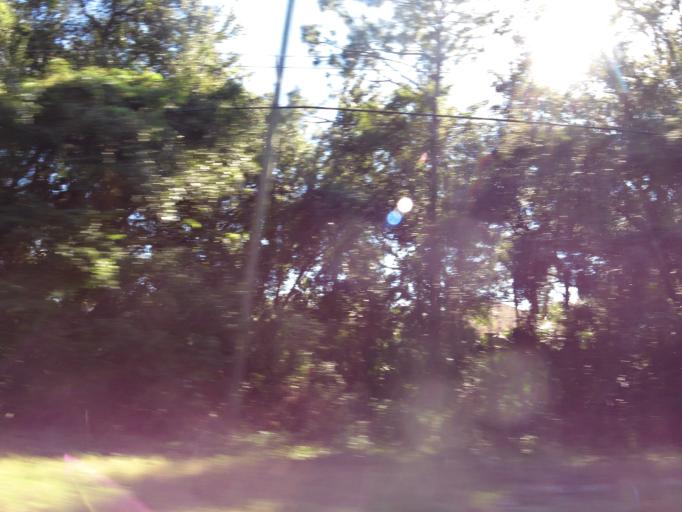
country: US
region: Florida
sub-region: Duval County
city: Atlantic Beach
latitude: 30.3975
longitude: -81.5010
